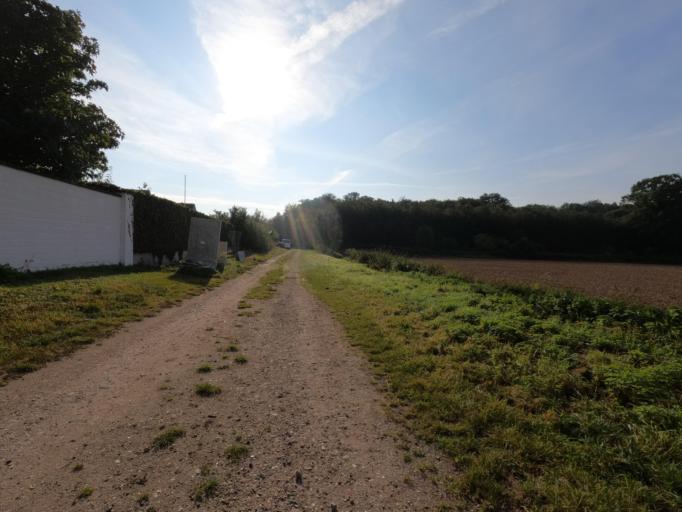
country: DE
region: North Rhine-Westphalia
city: Huckelhoven
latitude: 51.0415
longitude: 6.2377
